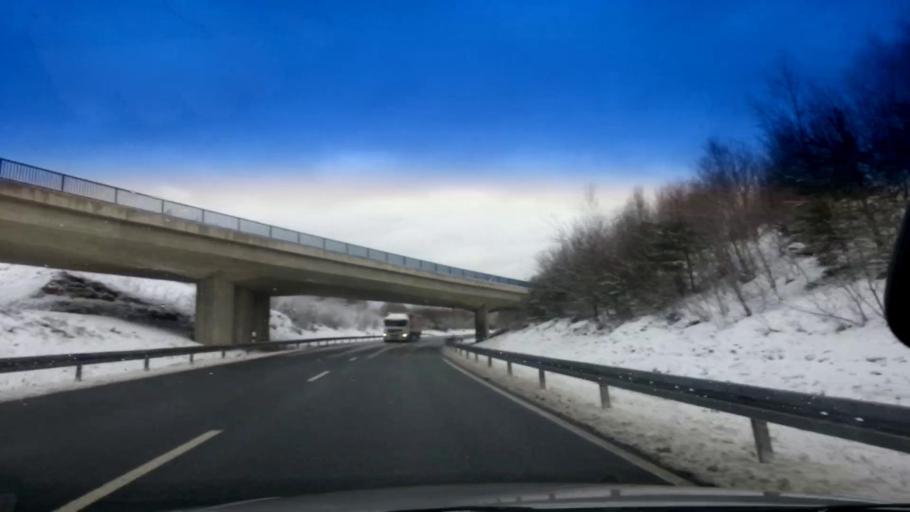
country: DE
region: Bavaria
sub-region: Upper Franconia
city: Selb
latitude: 50.1912
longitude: 12.1298
